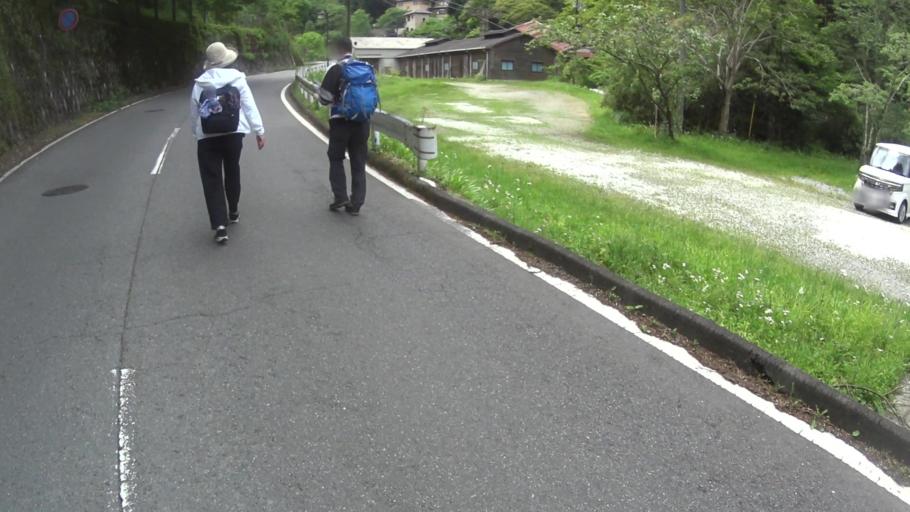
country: JP
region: Nara
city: Yoshino-cho
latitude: 34.3740
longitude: 135.8560
